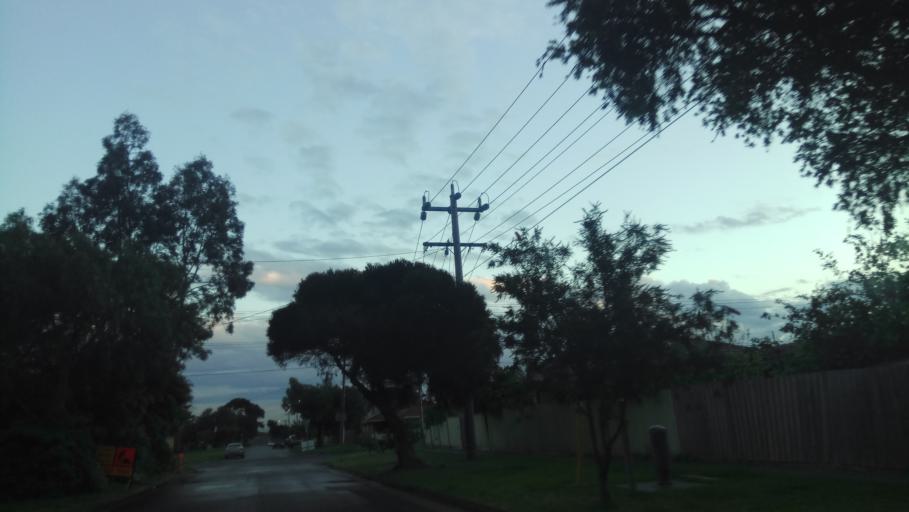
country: AU
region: Victoria
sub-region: Hobsons Bay
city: Laverton
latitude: -37.8659
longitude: 144.7772
